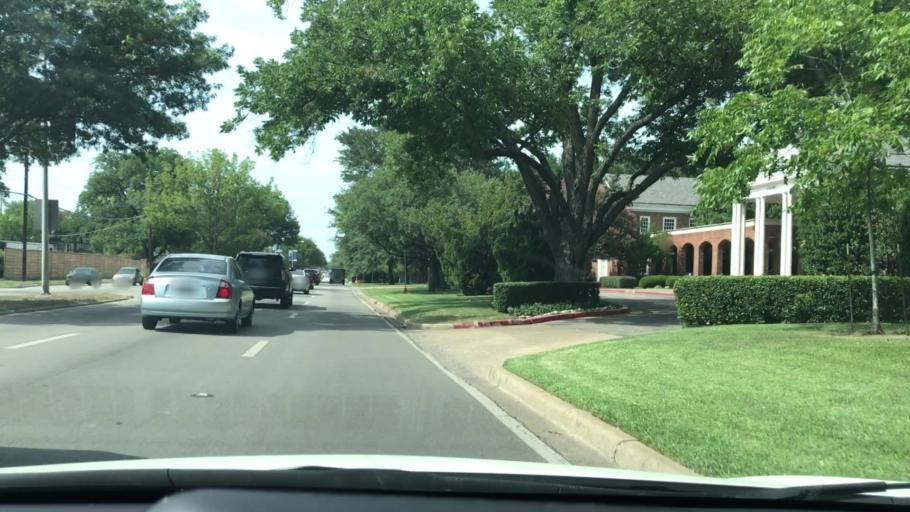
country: US
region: Texas
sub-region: Dallas County
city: University Park
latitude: 32.8807
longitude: -96.8039
